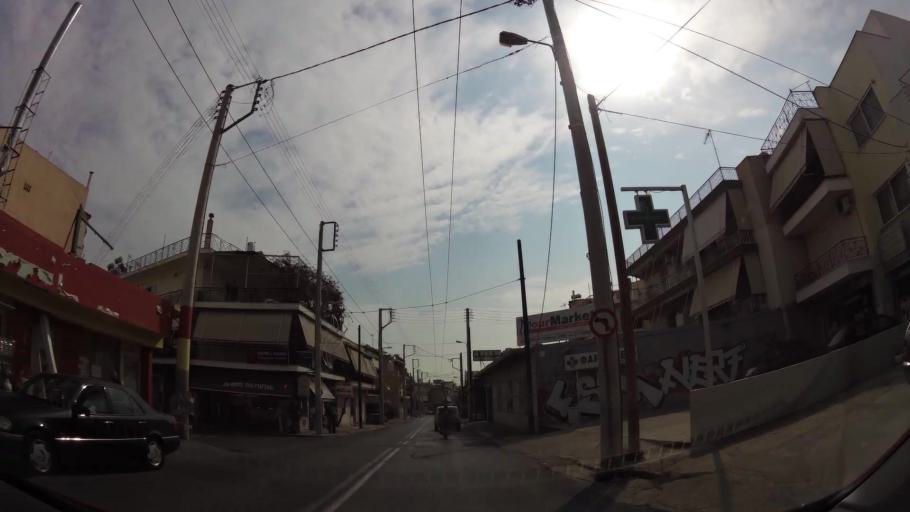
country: GR
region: Attica
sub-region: Nomarchia Athinas
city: Peristeri
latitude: 38.0234
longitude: 23.6843
